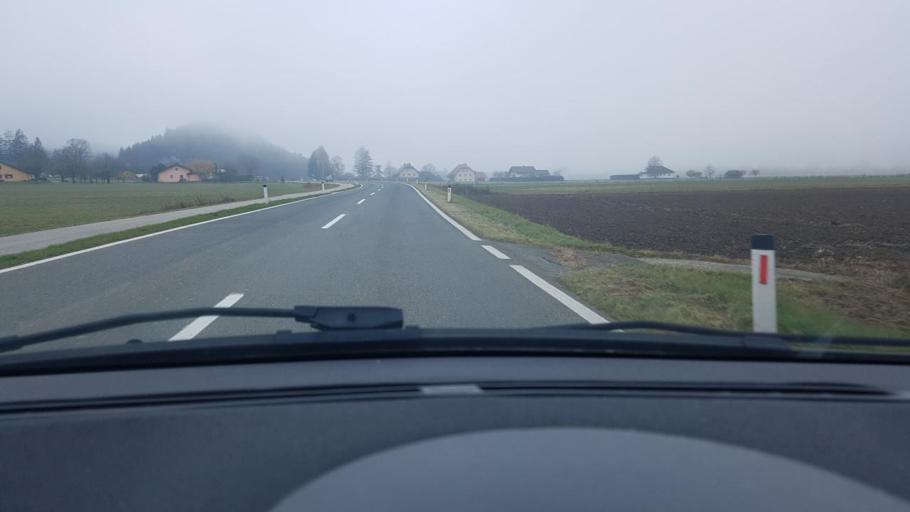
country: AT
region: Carinthia
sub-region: Politischer Bezirk Volkermarkt
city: Neuhaus
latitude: 46.6438
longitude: 14.8523
